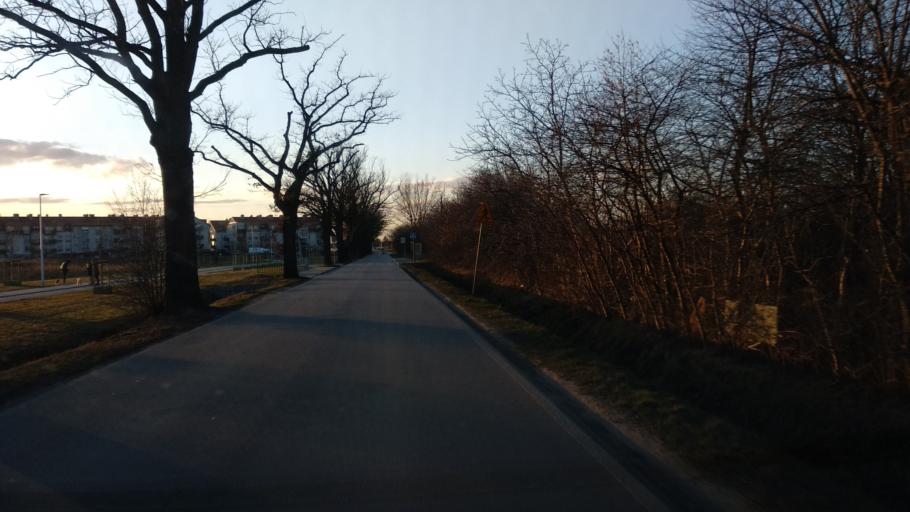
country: PL
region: Lower Silesian Voivodeship
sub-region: Powiat wroclawski
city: Zerniki Wroclawskie
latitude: 51.0660
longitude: 17.0607
